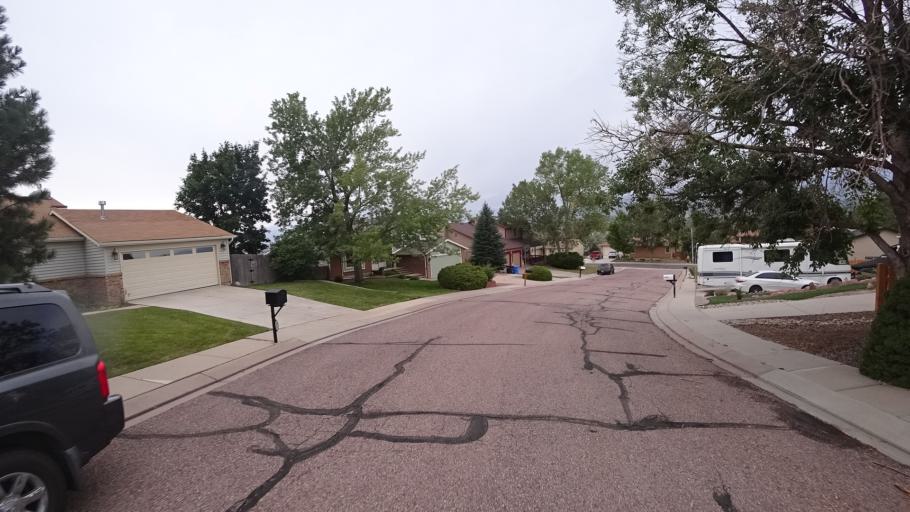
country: US
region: Colorado
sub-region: El Paso County
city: Colorado Springs
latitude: 38.9202
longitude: -104.8116
